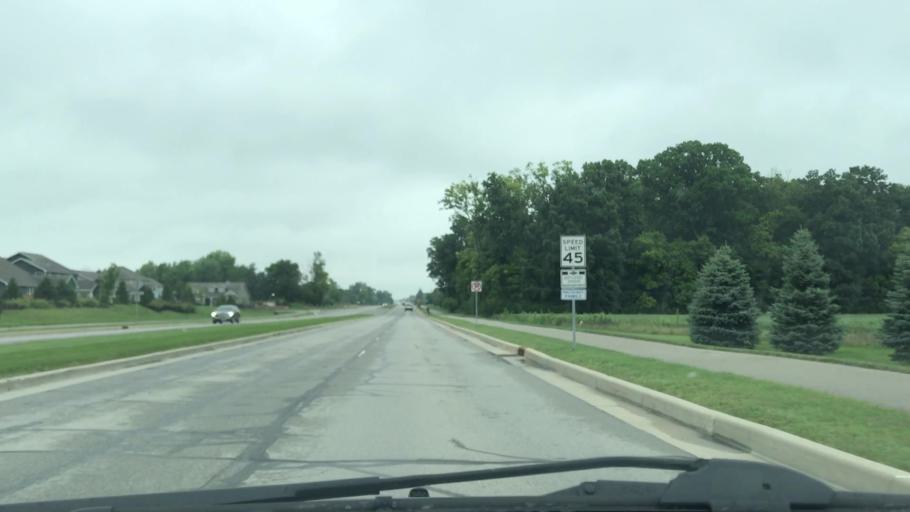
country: US
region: Indiana
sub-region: Hamilton County
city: Westfield
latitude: 40.0231
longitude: -86.0705
